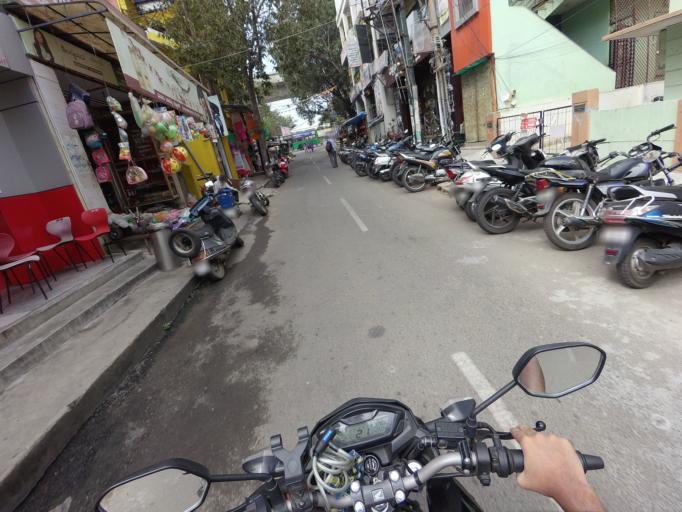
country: IN
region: Karnataka
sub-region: Bangalore Urban
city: Bangalore
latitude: 12.9716
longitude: 77.5383
